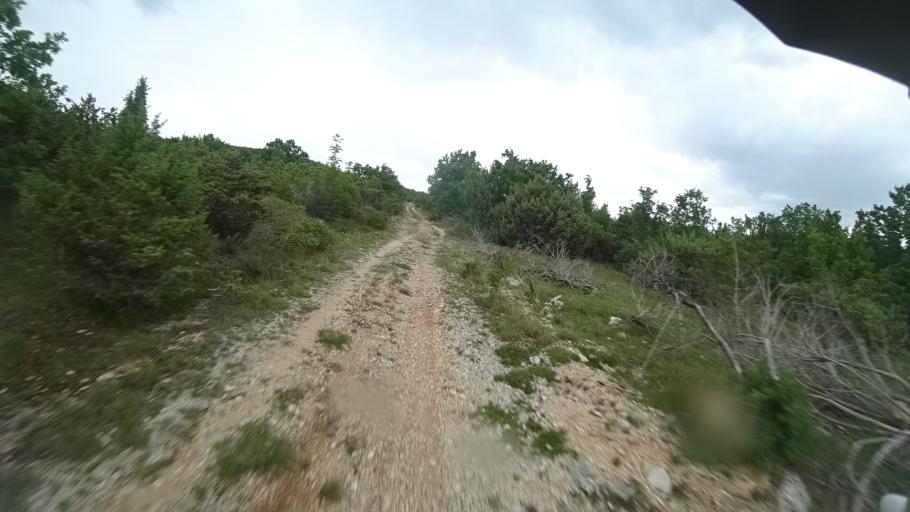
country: HR
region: Sibensko-Kniniska
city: Knin
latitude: 44.0276
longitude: 16.2581
